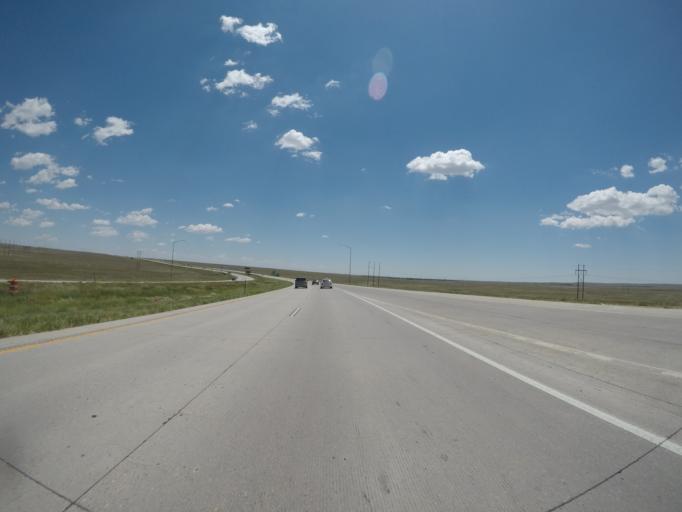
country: US
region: Colorado
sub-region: Lincoln County
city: Limon
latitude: 39.2623
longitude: -103.6645
